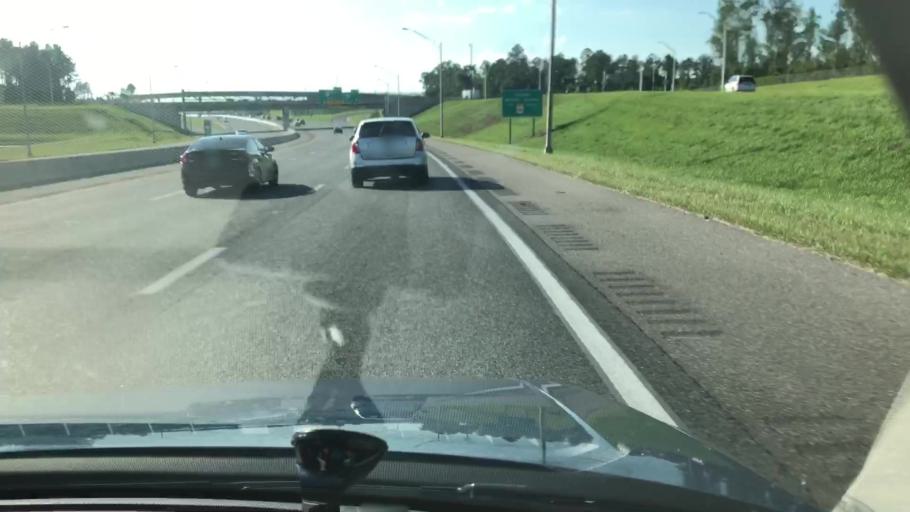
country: US
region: Florida
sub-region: Orange County
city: South Apopka
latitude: 28.6526
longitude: -81.5231
